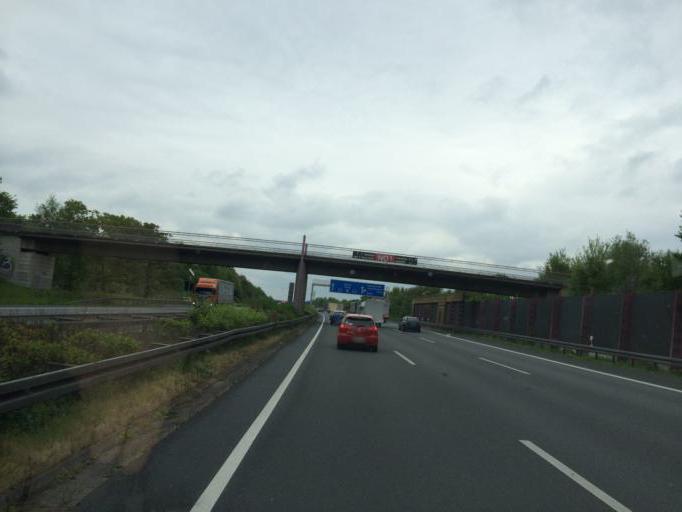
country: DE
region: Lower Saxony
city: Arpke
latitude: 52.3640
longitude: 10.1057
